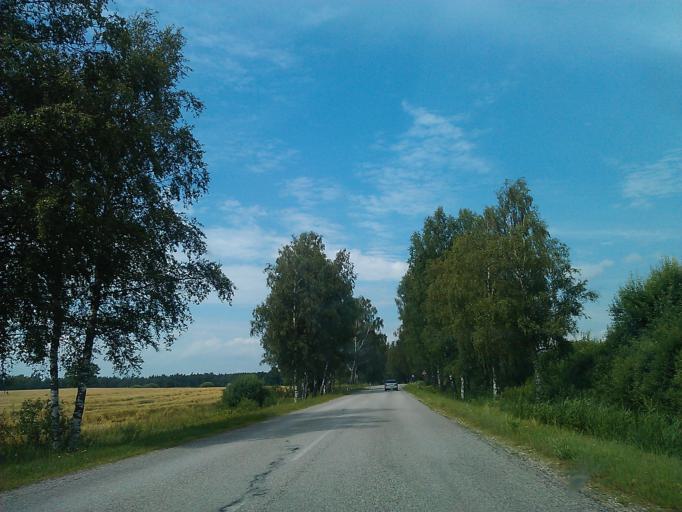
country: LV
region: Burtnieki
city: Matisi
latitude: 57.6764
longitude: 25.1981
